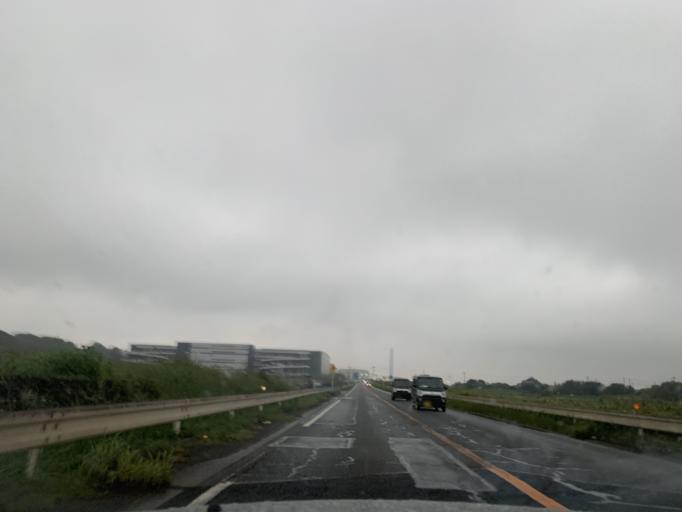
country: JP
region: Chiba
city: Nagareyama
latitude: 35.8917
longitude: 139.8942
